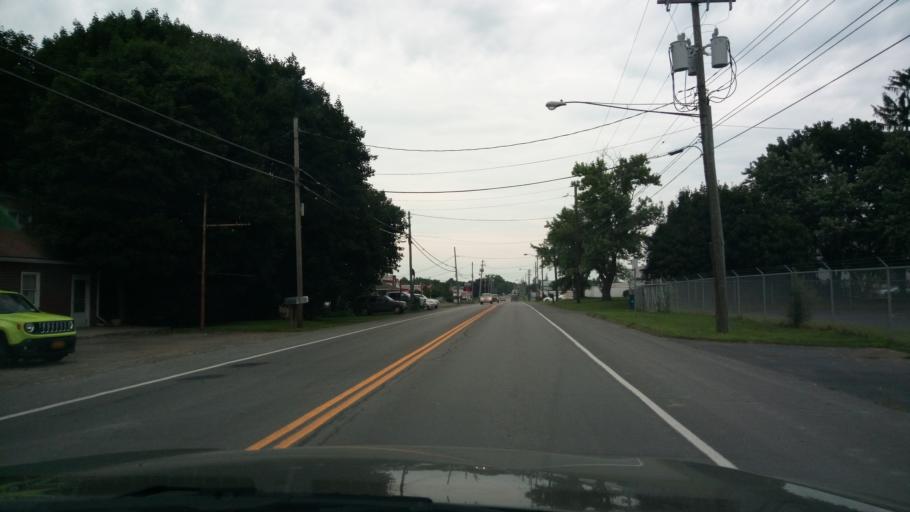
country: US
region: New York
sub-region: Chemung County
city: Elmira Heights
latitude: 42.1404
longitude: -76.8139
